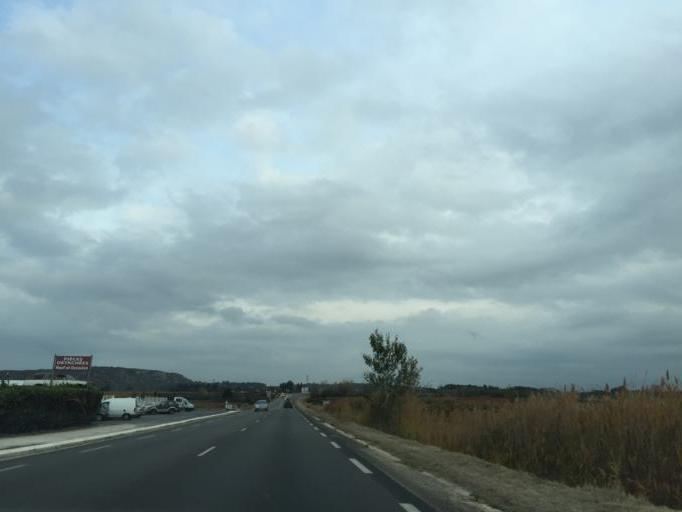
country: FR
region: Languedoc-Roussillon
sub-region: Departement du Gard
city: Remoulins
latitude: 43.9397
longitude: 4.5887
